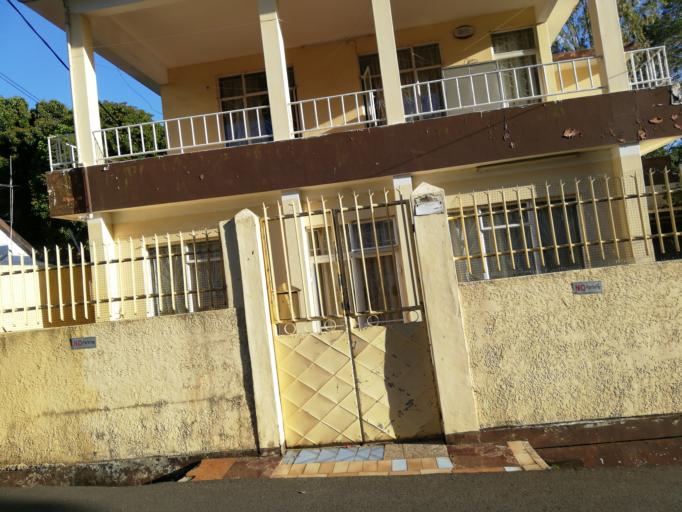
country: MU
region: Moka
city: Moka
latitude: -20.2229
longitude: 57.4699
